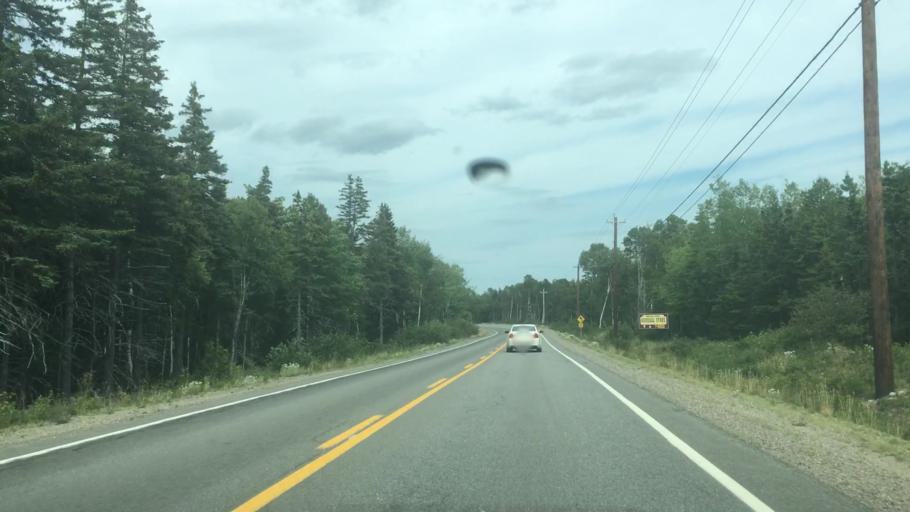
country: CA
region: Nova Scotia
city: Sydney Mines
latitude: 46.5071
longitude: -60.4328
